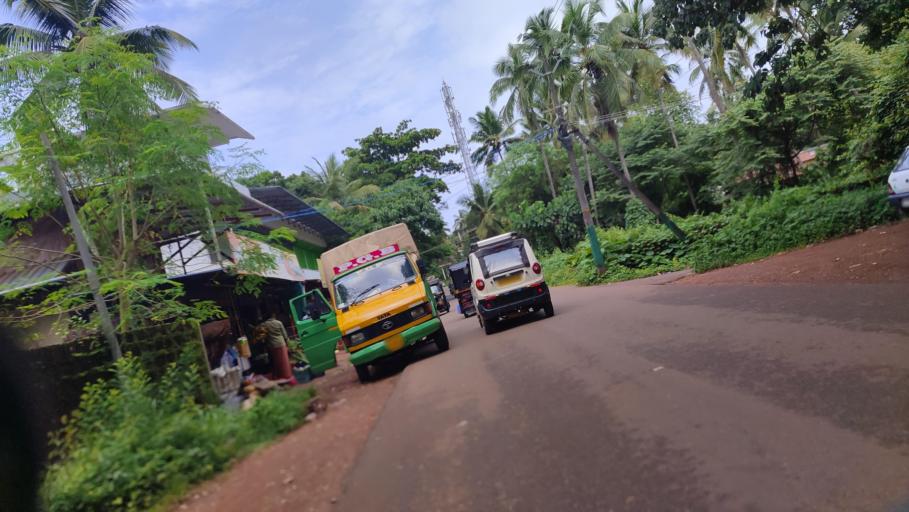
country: IN
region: Kerala
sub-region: Kasaragod District
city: Kannangad
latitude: 12.3920
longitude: 75.0444
